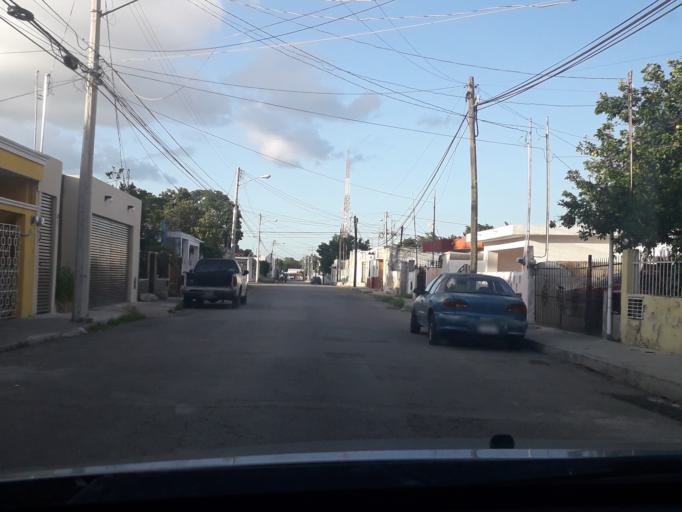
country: MX
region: Yucatan
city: Merida
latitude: 20.9694
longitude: -89.6457
